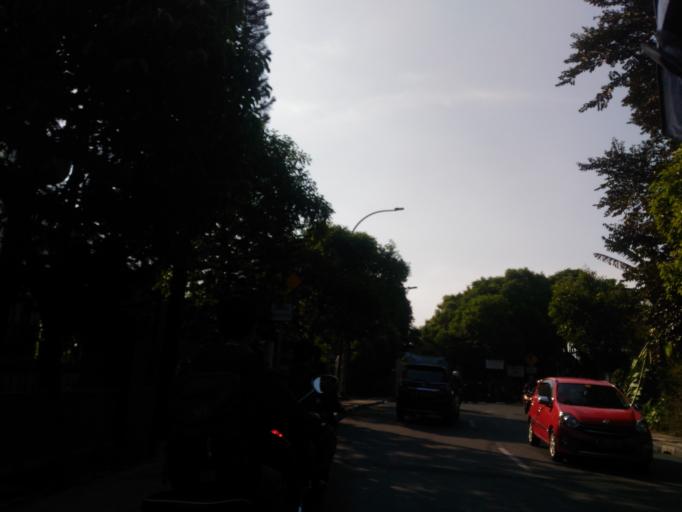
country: ID
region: West Java
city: Depok
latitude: -6.3121
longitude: 106.8599
